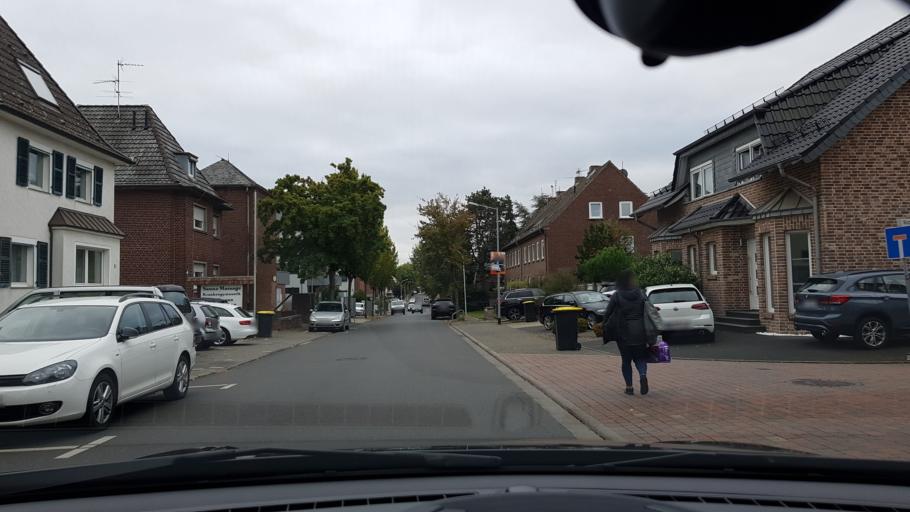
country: DE
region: North Rhine-Westphalia
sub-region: Regierungsbezirk Koln
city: Bergheim
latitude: 50.9570
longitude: 6.6466
